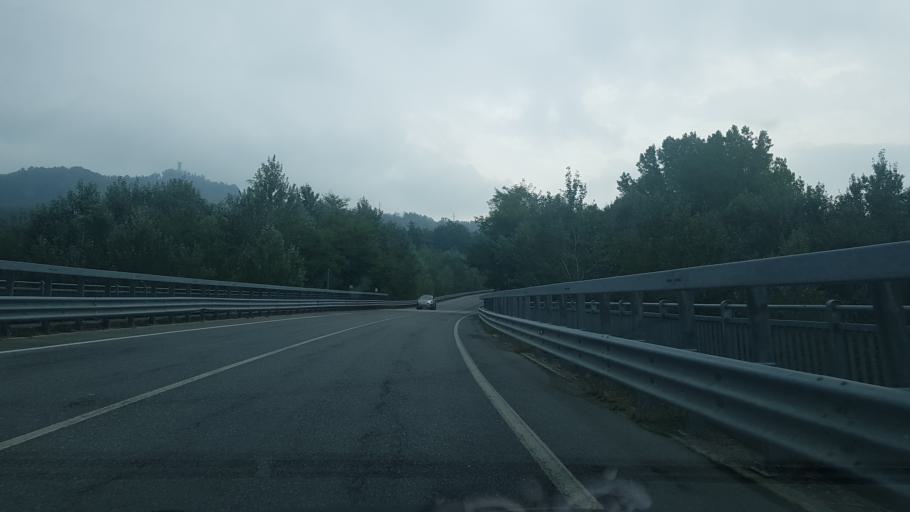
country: IT
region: Piedmont
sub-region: Provincia di Cuneo
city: Rocca Ciglie
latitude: 44.4265
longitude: 7.9561
